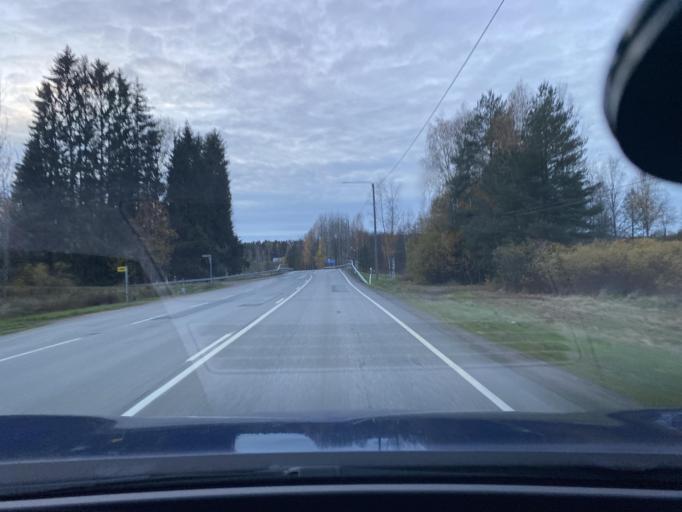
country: FI
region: Uusimaa
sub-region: Helsinki
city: Saukkola
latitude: 60.3895
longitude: 24.0348
